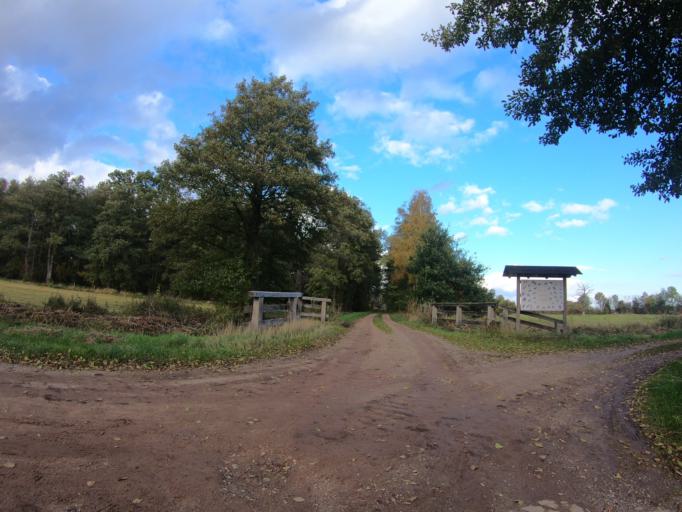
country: DE
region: Lower Saxony
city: Wagenhoff
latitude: 52.5470
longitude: 10.5603
